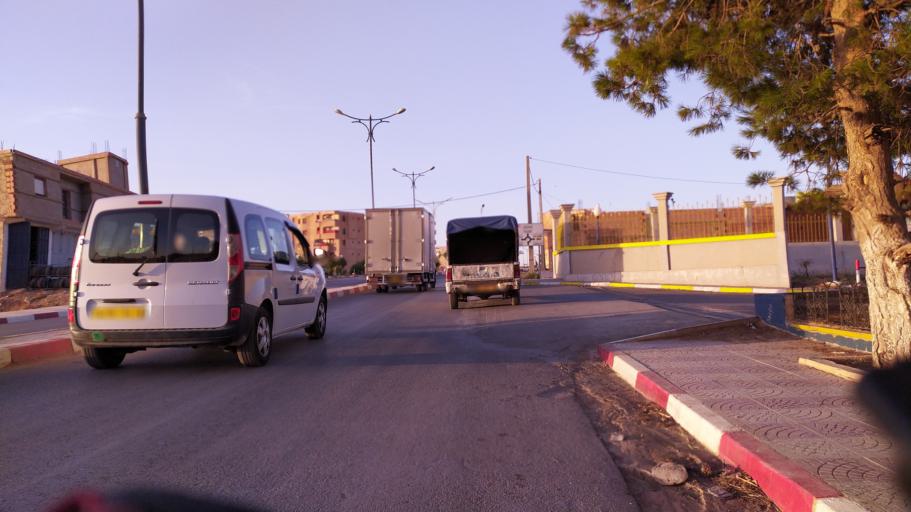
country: DZ
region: Tiaret
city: Frenda
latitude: 34.8962
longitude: 1.2477
